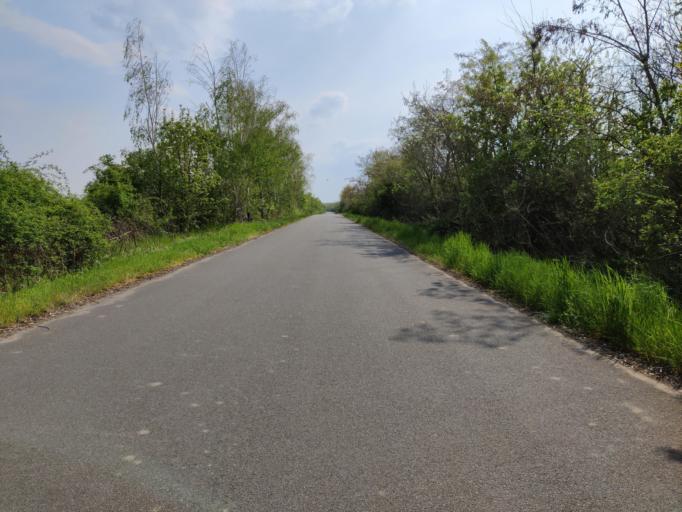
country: DE
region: Saxony
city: Bohlen
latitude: 51.2252
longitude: 12.3654
